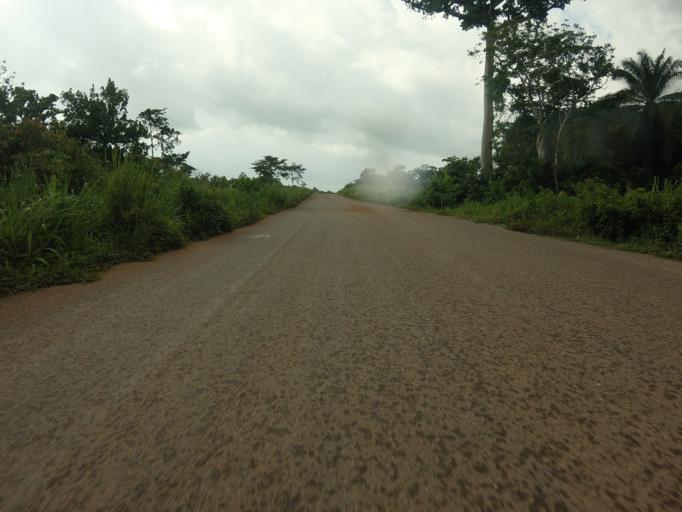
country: TG
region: Plateaux
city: Kpalime
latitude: 6.9260
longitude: 0.4617
